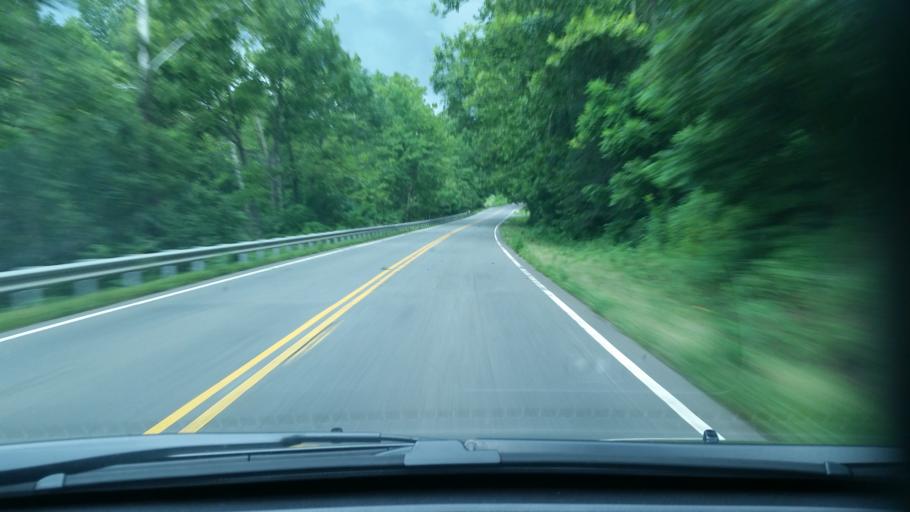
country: US
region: Virginia
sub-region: Nelson County
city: Nellysford
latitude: 37.8947
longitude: -78.8298
